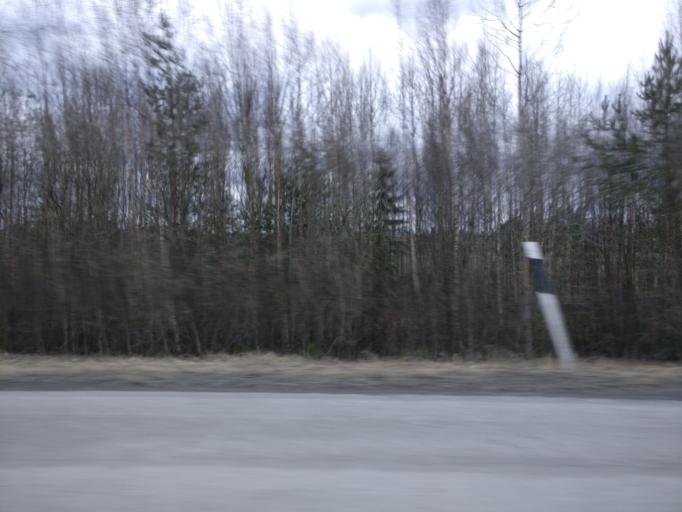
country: FI
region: Haeme
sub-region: Haemeenlinna
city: Parola
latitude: 61.0668
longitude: 24.3150
